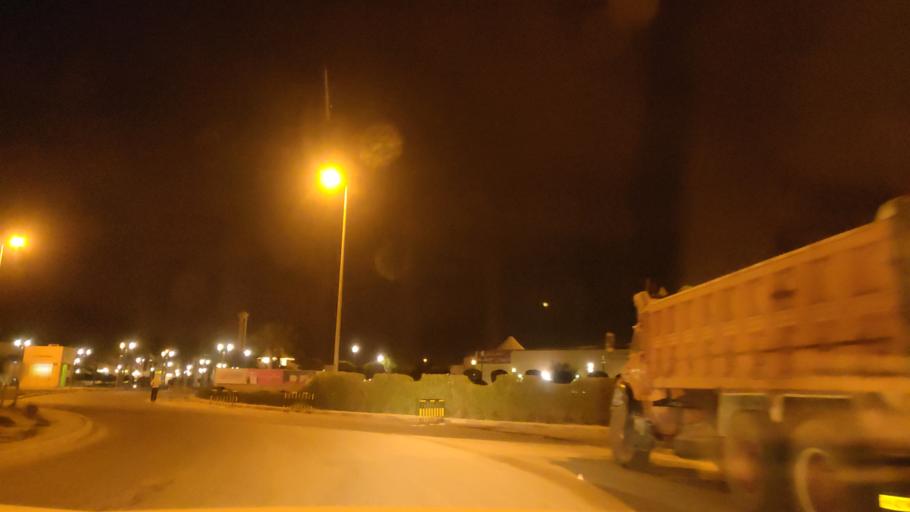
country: KW
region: Al Asimah
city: Ar Rabiyah
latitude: 29.2519
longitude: 47.8445
